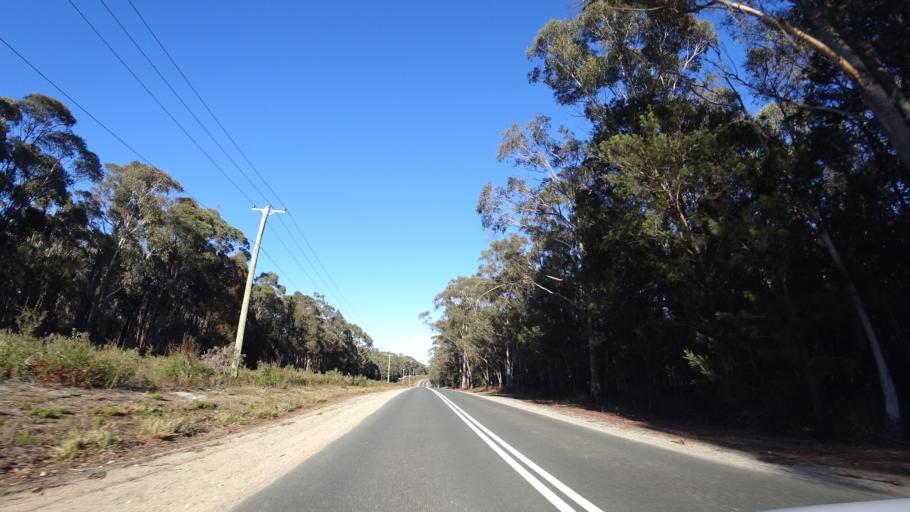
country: AU
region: Tasmania
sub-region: Break O'Day
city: St Helens
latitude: -41.2823
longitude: 148.1530
